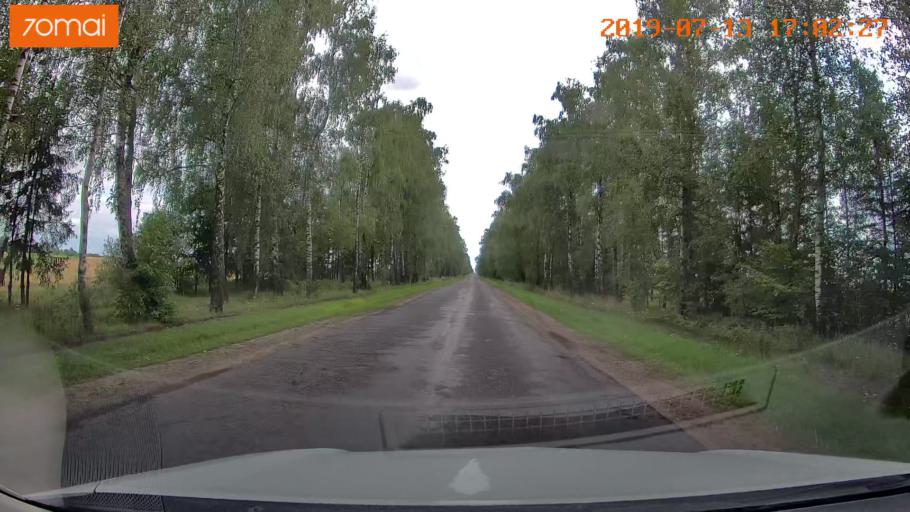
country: BY
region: Mogilev
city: Kirawsk
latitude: 53.2858
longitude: 29.3868
